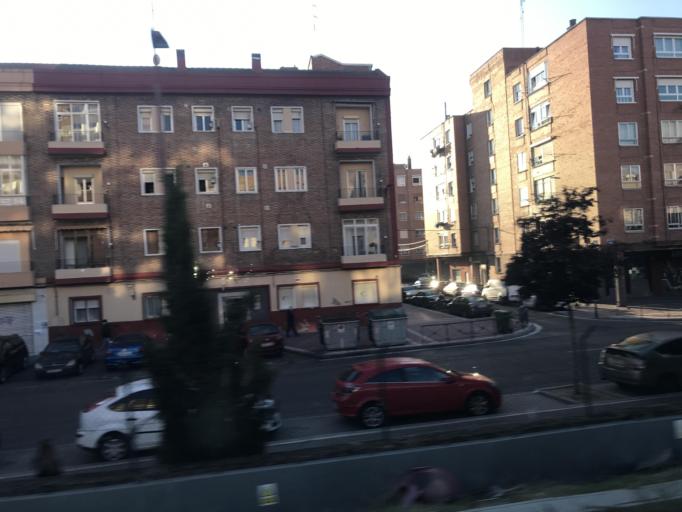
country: ES
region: Castille and Leon
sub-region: Provincia de Valladolid
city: Valladolid
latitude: 41.6491
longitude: -4.7115
